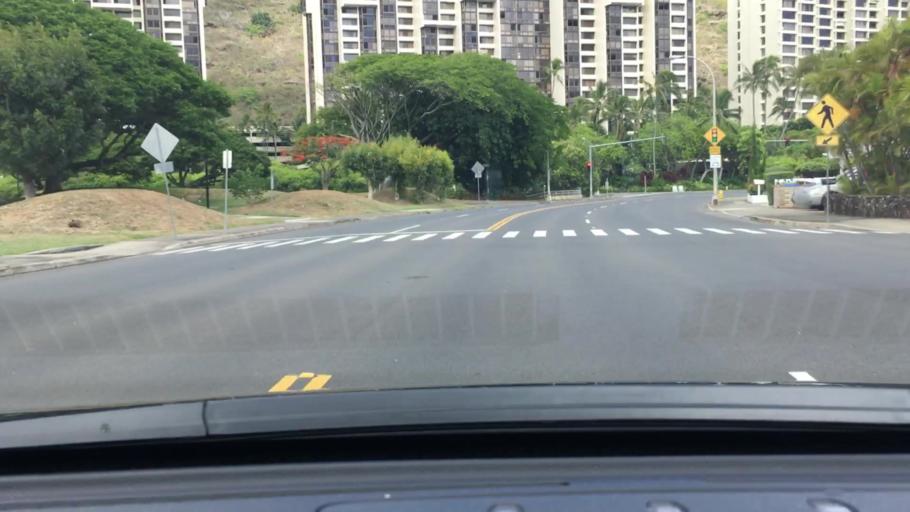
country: US
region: Hawaii
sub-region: Honolulu County
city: Waimanalo Beach
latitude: 21.2938
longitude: -157.7094
